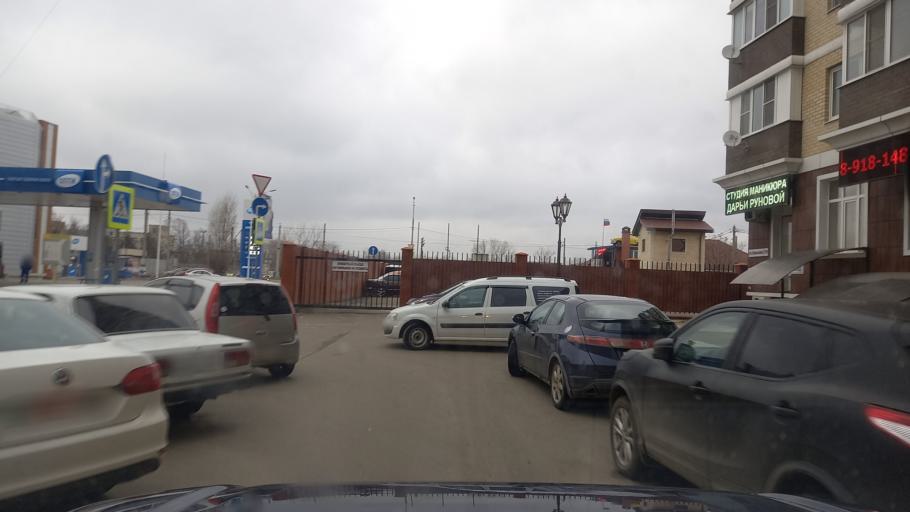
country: RU
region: Krasnodarskiy
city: Pashkovskiy
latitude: 45.0409
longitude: 39.0964
